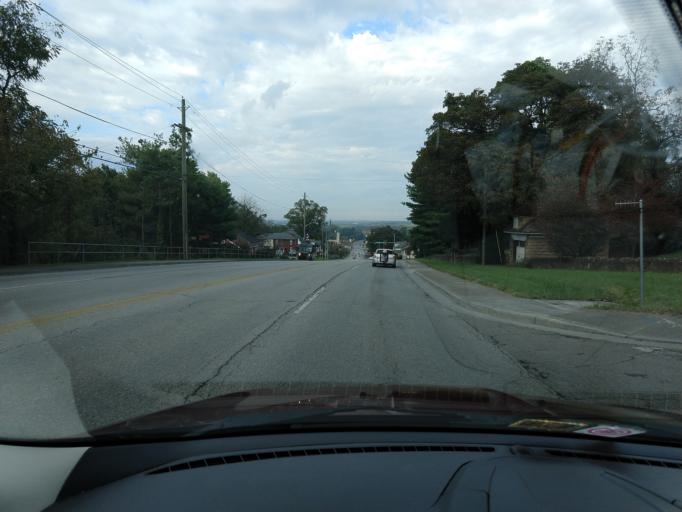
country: US
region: Virginia
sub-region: Roanoke County
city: Vinton
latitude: 37.2794
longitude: -79.8884
